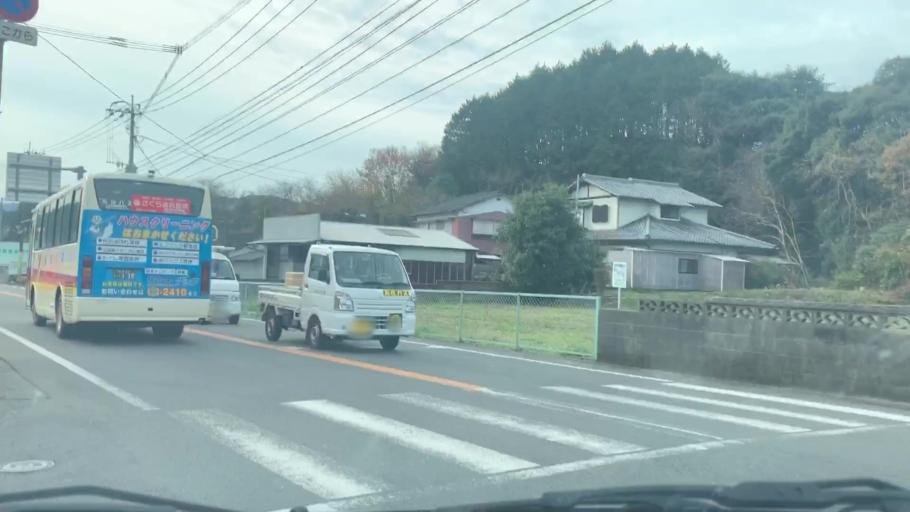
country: JP
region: Saga Prefecture
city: Ureshinomachi-shimojuku
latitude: 33.1193
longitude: 130.0009
